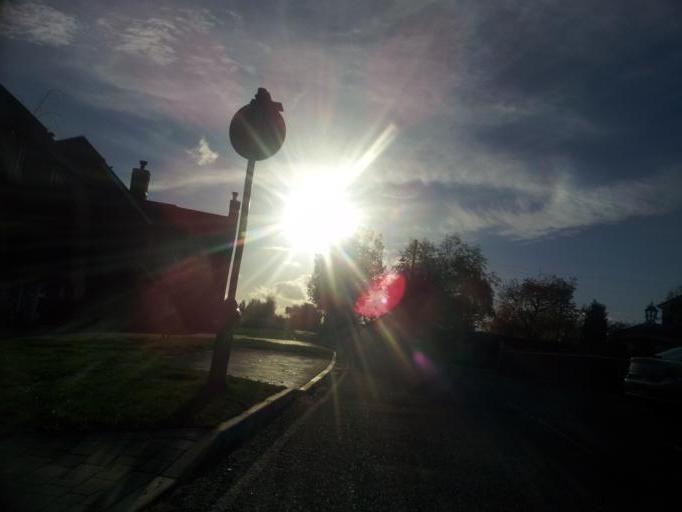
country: GB
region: England
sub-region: Kent
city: Sittingbourne
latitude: 51.3758
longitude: 0.7216
